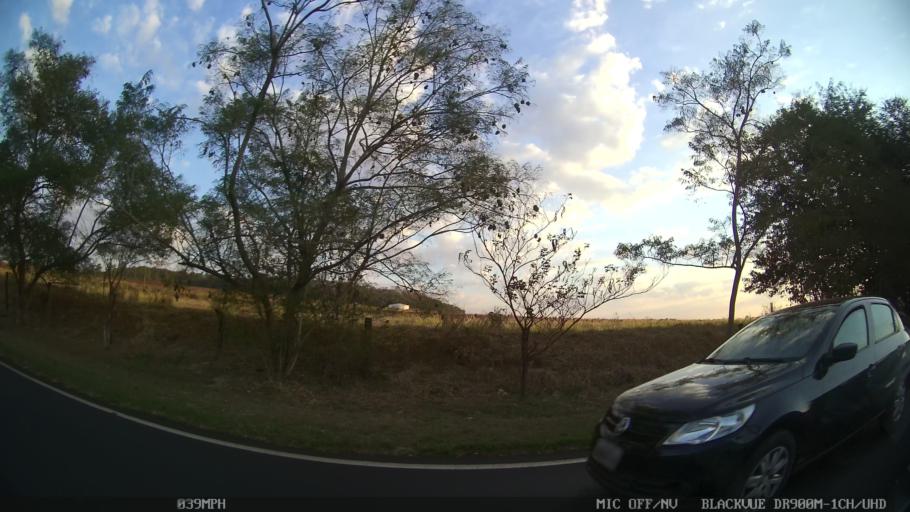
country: BR
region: Sao Paulo
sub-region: Ribeirao Preto
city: Ribeirao Preto
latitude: -21.1572
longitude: -47.7734
